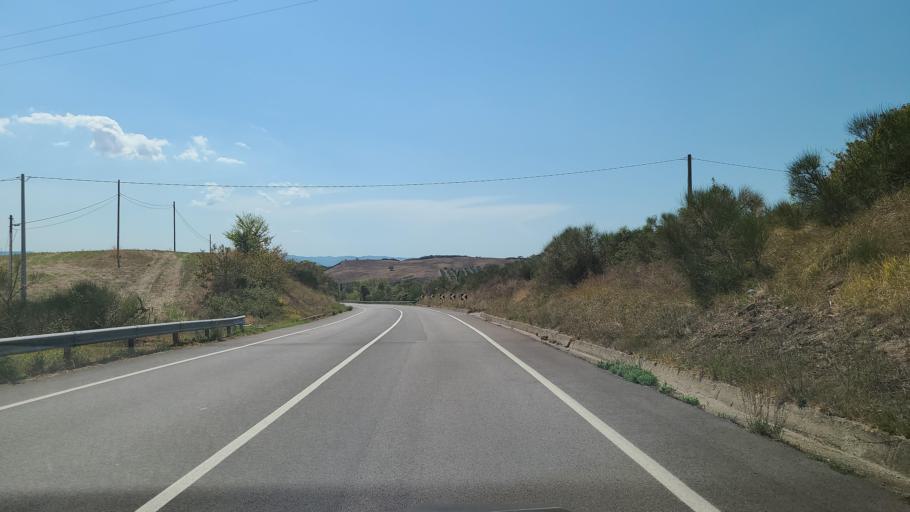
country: IT
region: Tuscany
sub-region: Province of Pisa
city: Volterra
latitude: 43.3865
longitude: 10.9407
